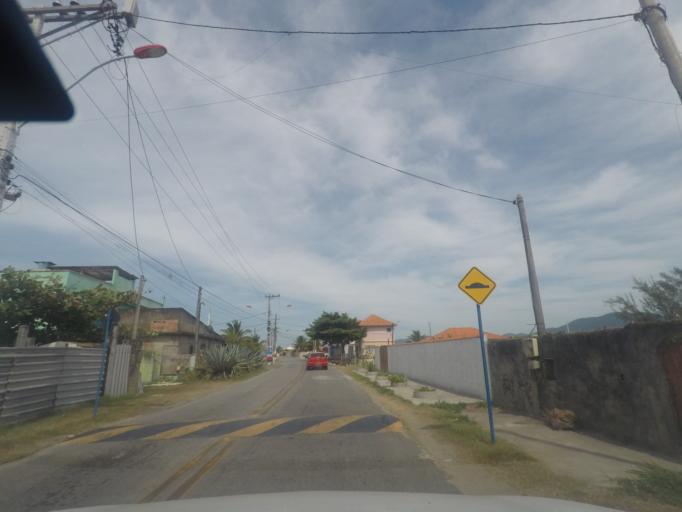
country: BR
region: Rio de Janeiro
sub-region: Marica
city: Marica
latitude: -22.9561
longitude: -42.6974
